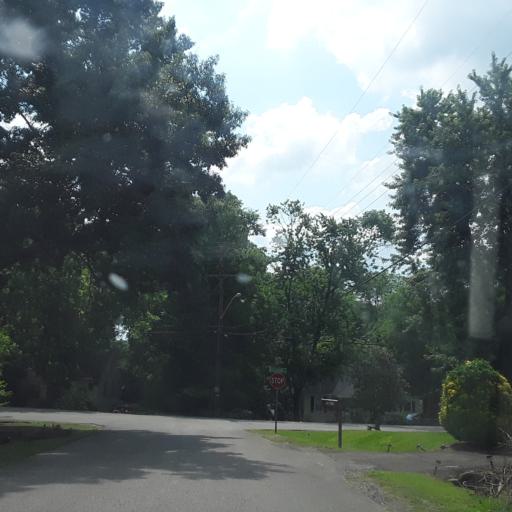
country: US
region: Tennessee
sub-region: Davidson County
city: Oak Hill
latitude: 36.1107
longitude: -86.7316
